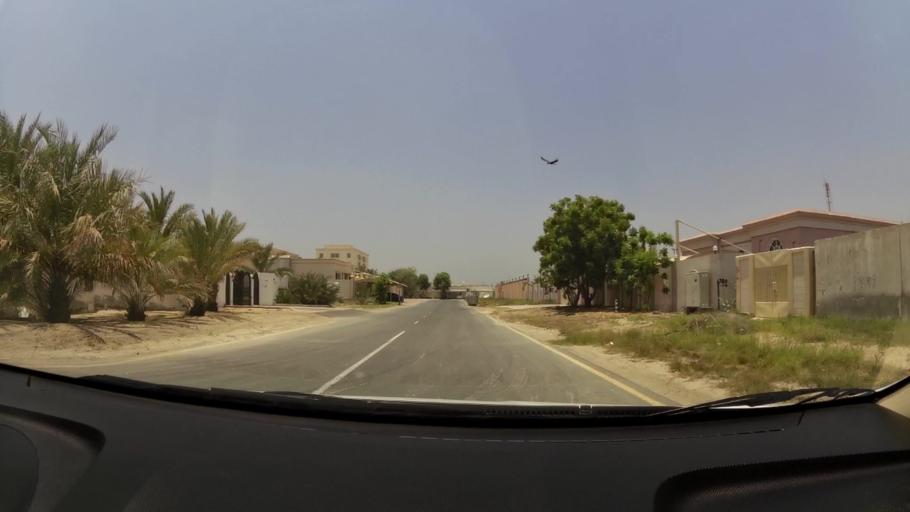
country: AE
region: Umm al Qaywayn
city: Umm al Qaywayn
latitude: 25.5360
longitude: 55.5418
